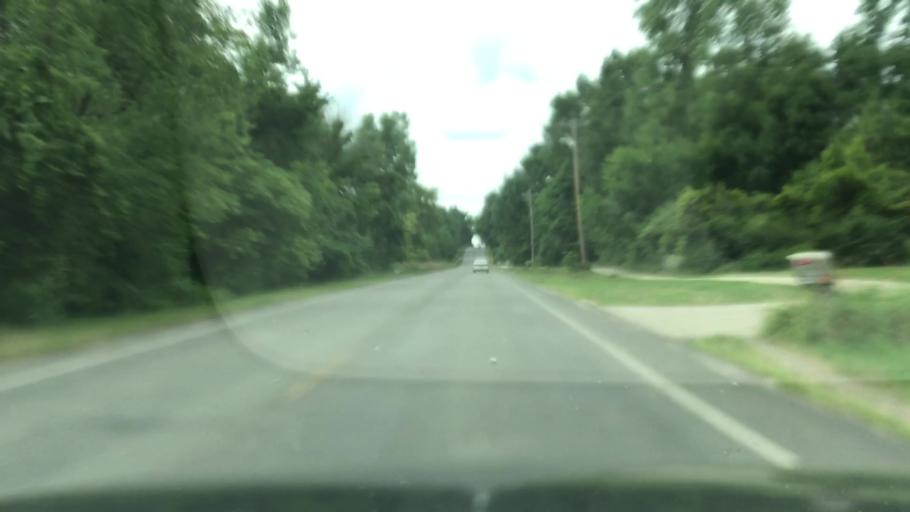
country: US
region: Michigan
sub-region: Kent County
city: East Grand Rapids
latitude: 42.9719
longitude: -85.5610
